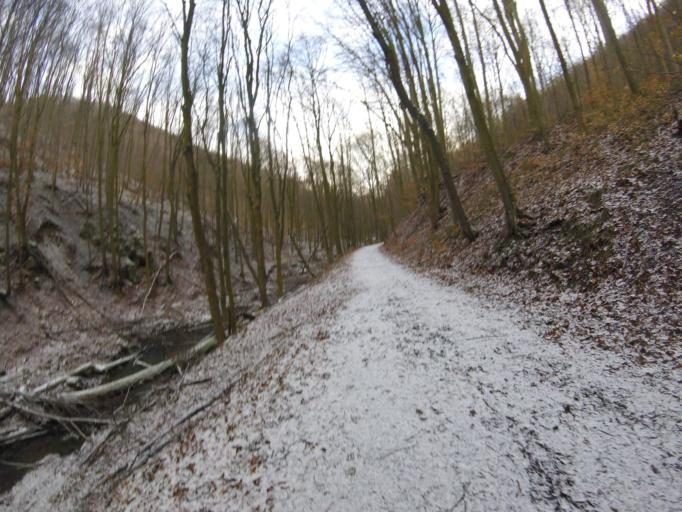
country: HU
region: Pest
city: Visegrad
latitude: 47.7545
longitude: 18.9886
